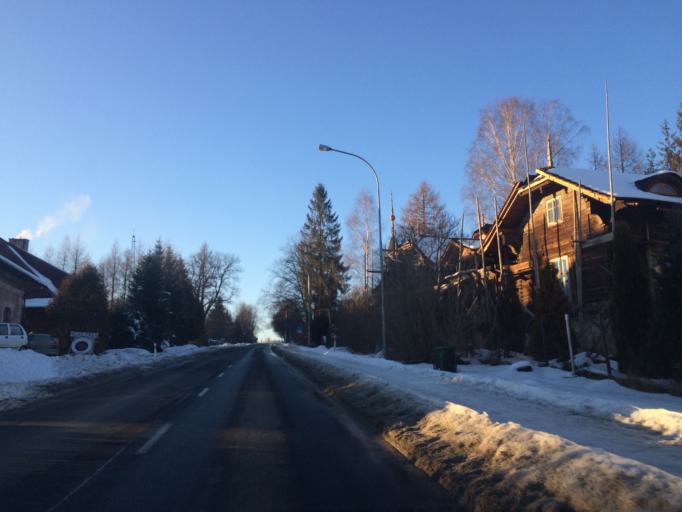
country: PL
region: Subcarpathian Voivodeship
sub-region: Powiat bieszczadzki
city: Lutowiska
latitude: 49.2521
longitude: 22.6940
